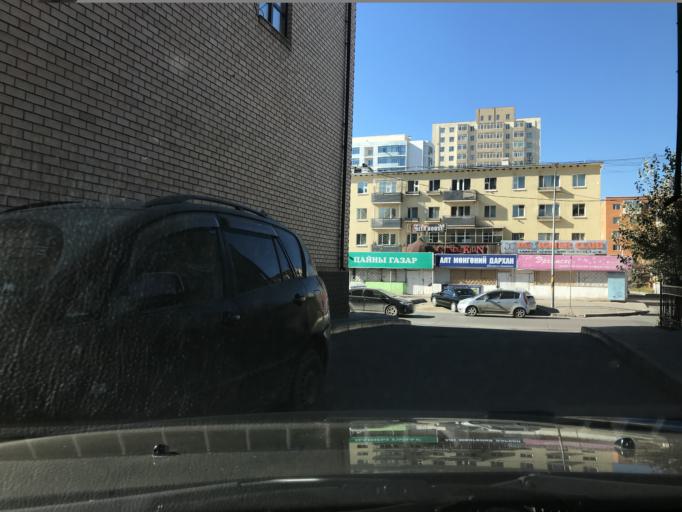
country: MN
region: Ulaanbaatar
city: Ulaanbaatar
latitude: 47.9186
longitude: 106.9072
